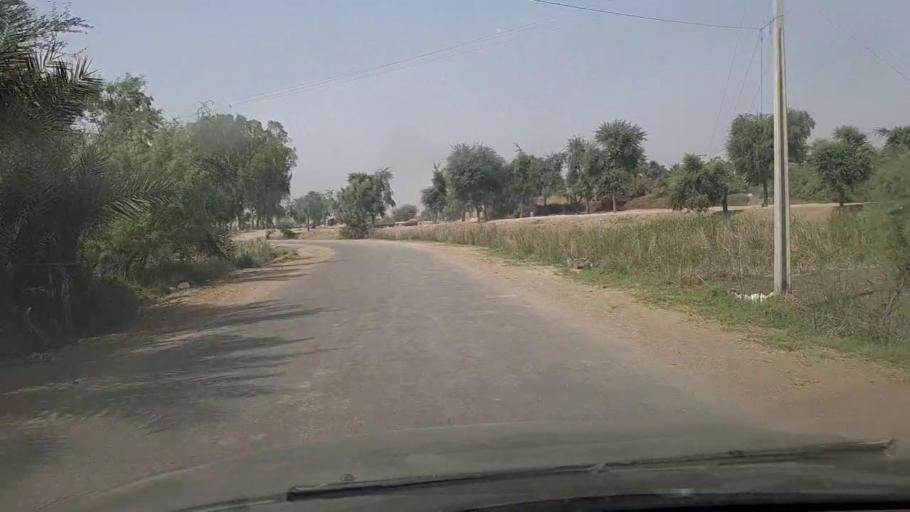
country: PK
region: Sindh
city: Khanpur
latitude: 27.8922
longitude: 69.4846
